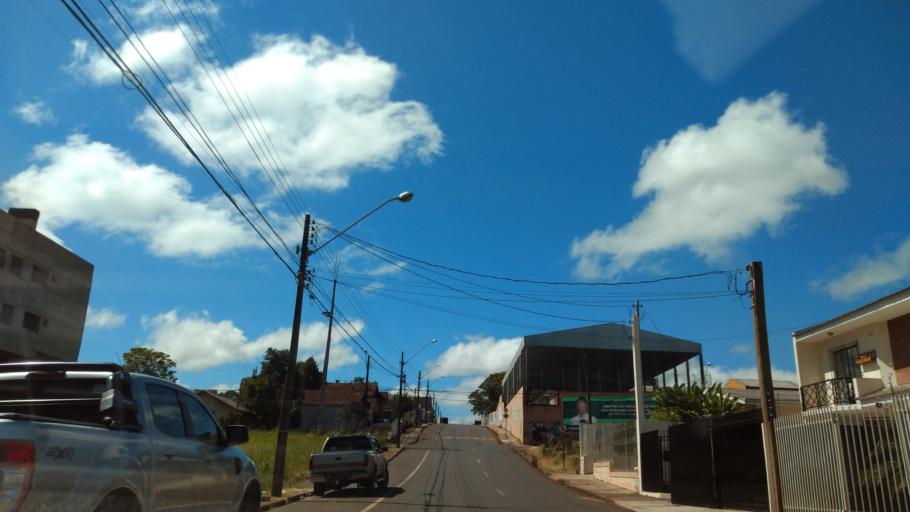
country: BR
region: Parana
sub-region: Guarapuava
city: Guarapuava
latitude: -25.3980
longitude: -51.4694
